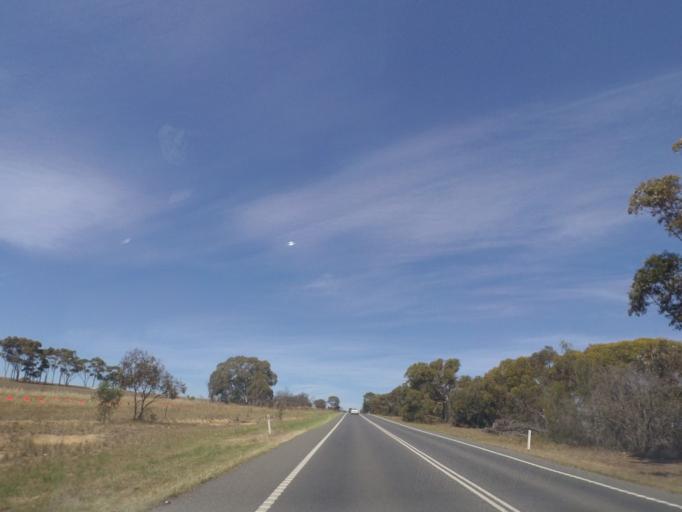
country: AU
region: Victoria
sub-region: Greater Geelong
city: Lara
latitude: -37.8866
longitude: 144.3754
